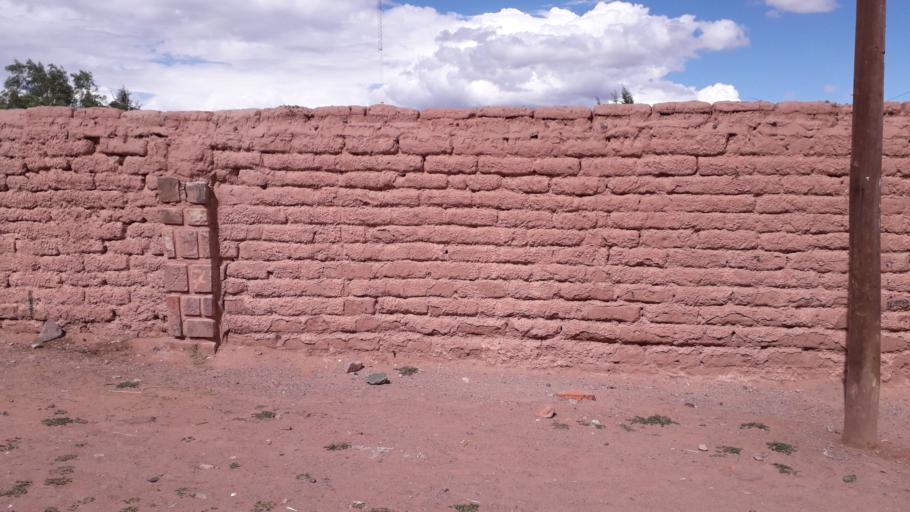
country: AR
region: Jujuy
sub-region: Departamento de Humahuaca
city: Humahuaca
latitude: -23.3045
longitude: -65.3568
